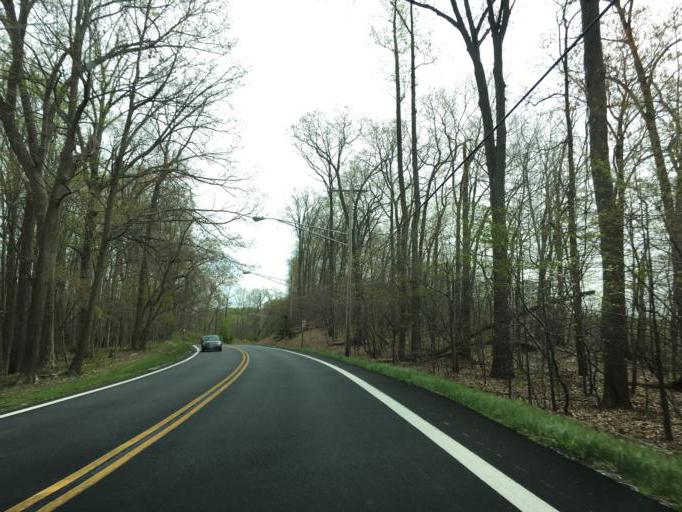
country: US
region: Maryland
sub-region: Baltimore County
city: Hampton
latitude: 39.4758
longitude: -76.5746
